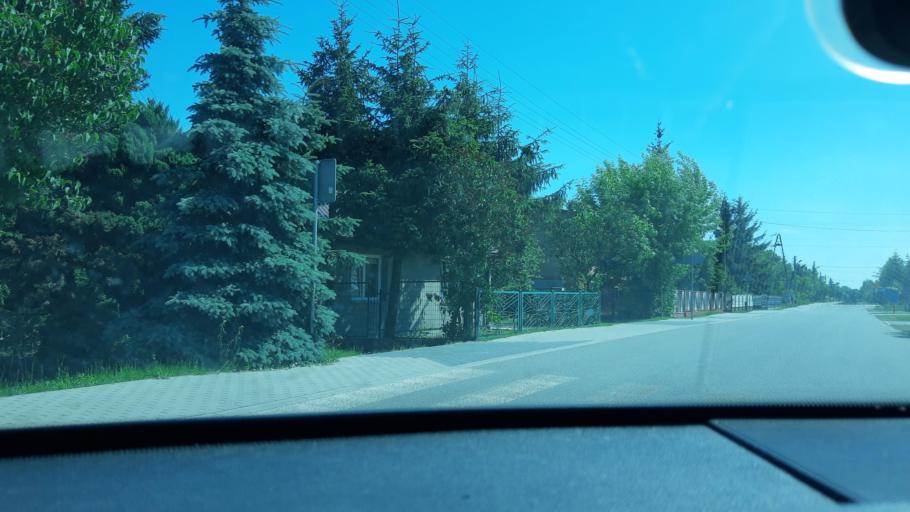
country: PL
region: Lodz Voivodeship
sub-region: Powiat zdunskowolski
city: Zdunska Wola
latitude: 51.6068
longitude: 18.9856
